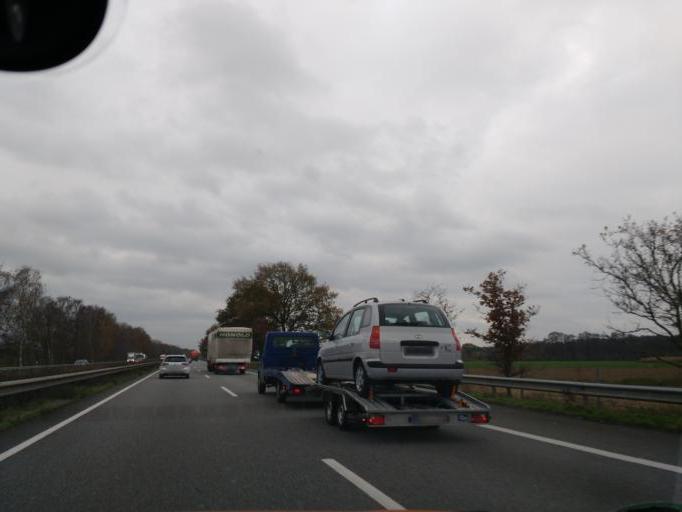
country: DE
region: Lower Saxony
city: Langwedel
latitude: 52.9788
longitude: 9.2201
